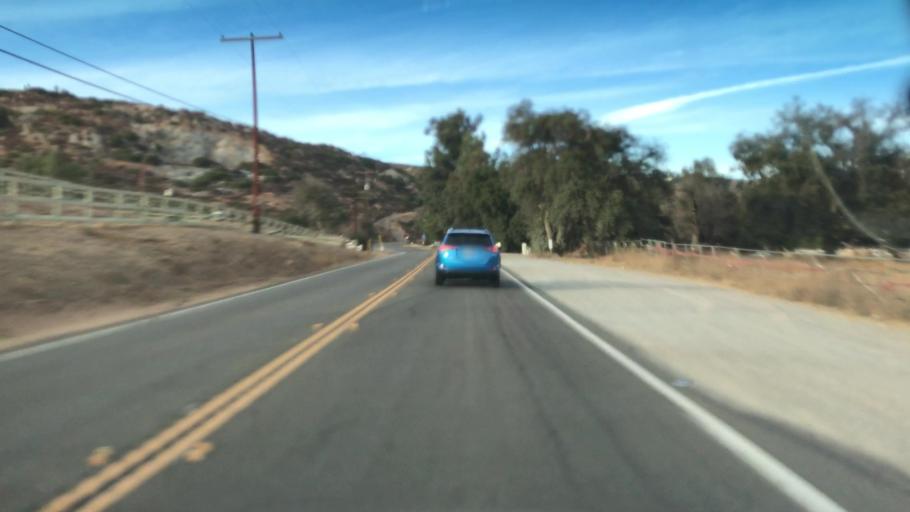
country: US
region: California
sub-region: San Diego County
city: Ramona
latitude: 33.0516
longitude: -116.8199
